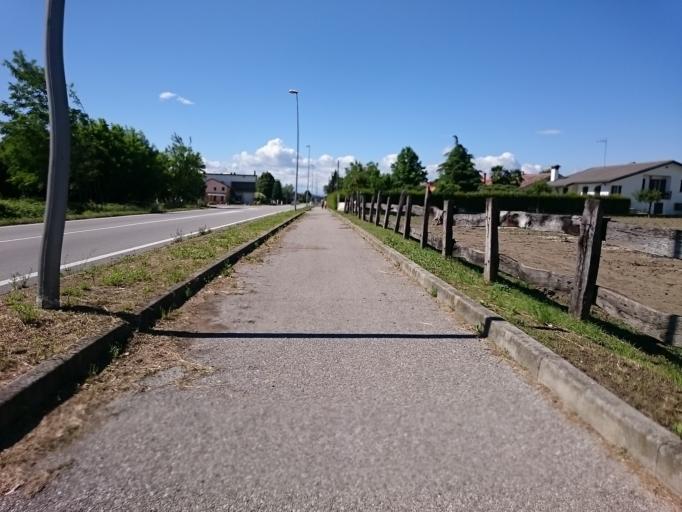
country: IT
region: Veneto
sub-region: Provincia di Venezia
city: Campolongo Maggiore
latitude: 45.3138
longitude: 12.0382
